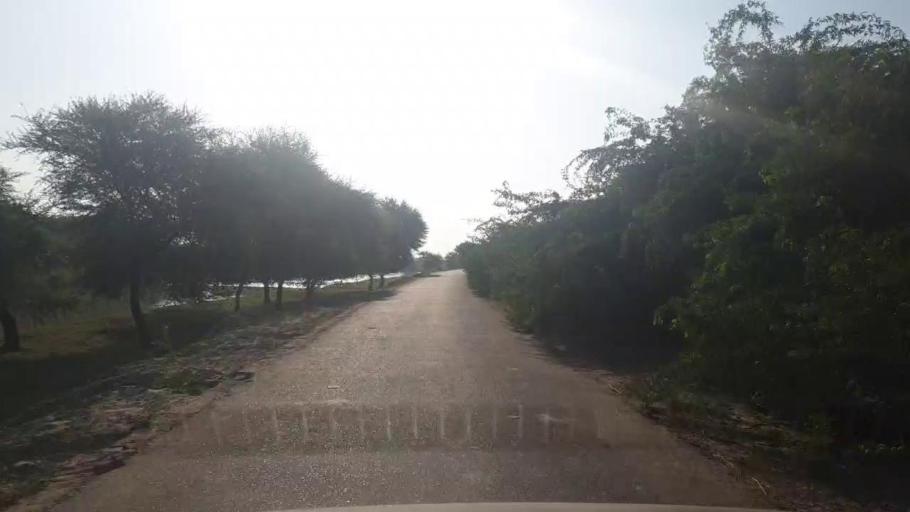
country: PK
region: Sindh
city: Tando Bago
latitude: 24.7324
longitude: 68.9347
